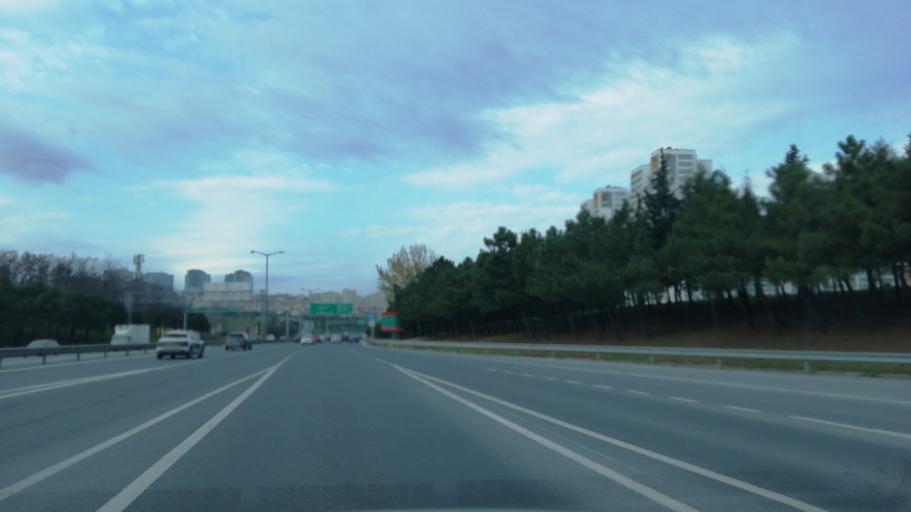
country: TR
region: Istanbul
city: Esenyurt
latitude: 41.0502
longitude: 28.6871
